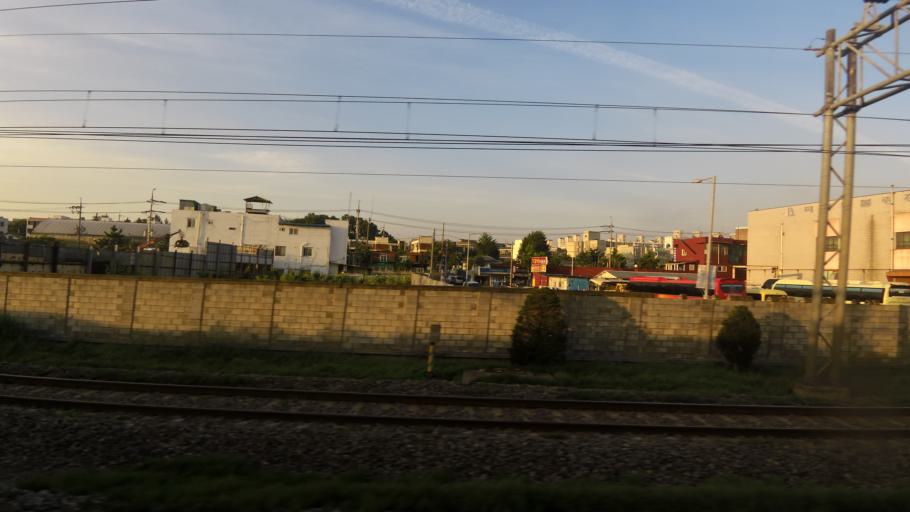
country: KR
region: Chungcheongnam-do
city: Seonghwan
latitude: 37.0018
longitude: 127.0749
